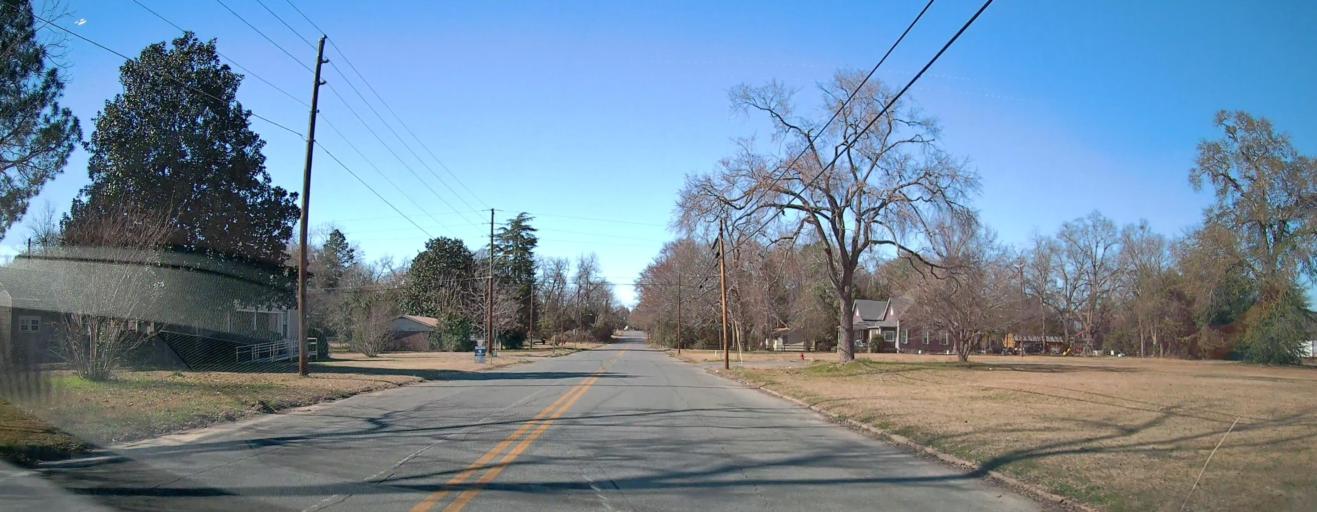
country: US
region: Georgia
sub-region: Macon County
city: Oglethorpe
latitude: 32.2958
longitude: -84.0609
